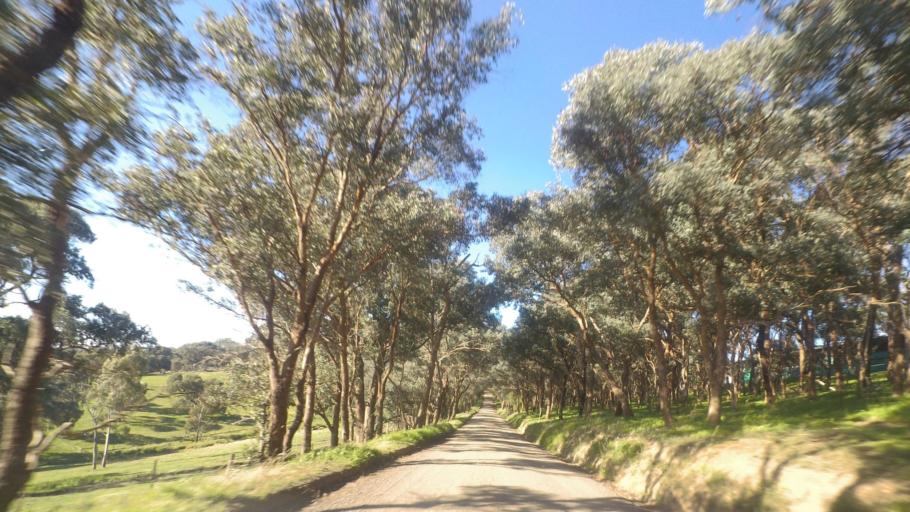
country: AU
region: Victoria
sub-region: Nillumbik
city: Research
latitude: -37.6928
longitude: 145.1921
